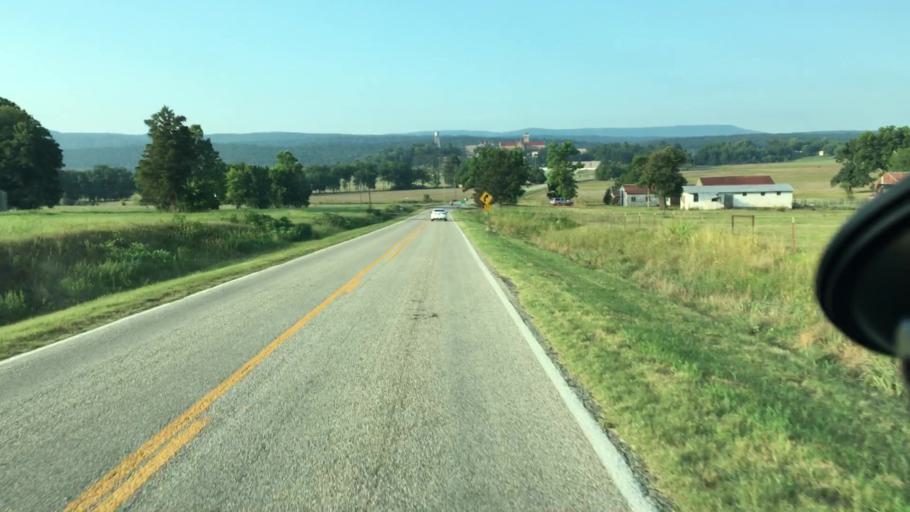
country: US
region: Arkansas
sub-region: Logan County
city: Paris
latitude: 35.3107
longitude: -93.6326
